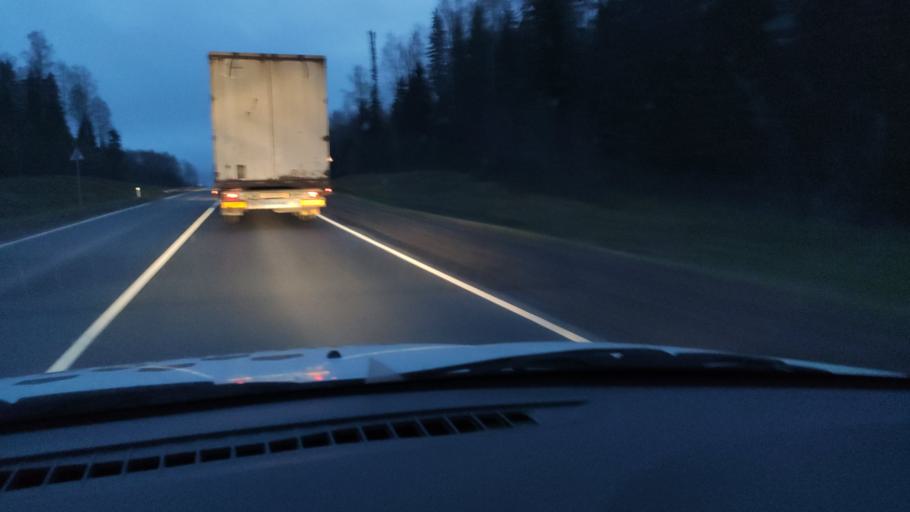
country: RU
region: Kirov
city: Kostino
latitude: 58.8332
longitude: 53.5033
